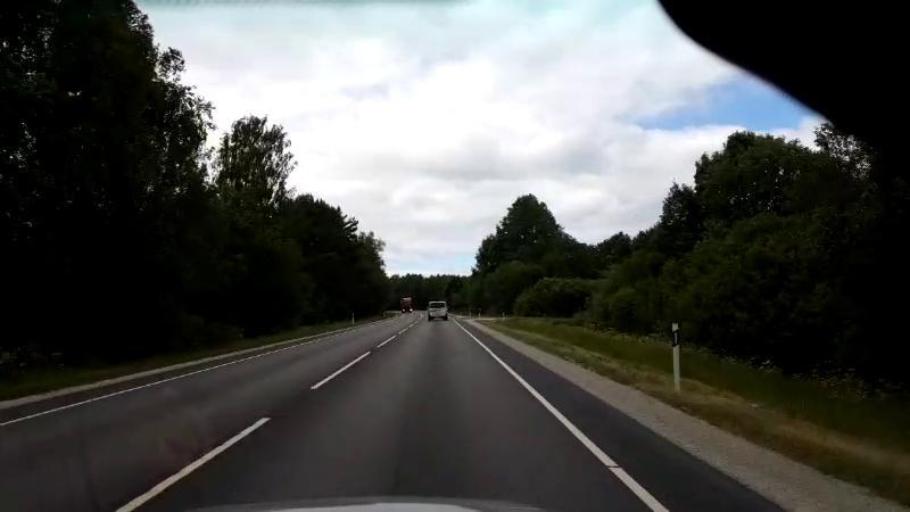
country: EE
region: Paernumaa
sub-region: Paernu linn
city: Parnu
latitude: 58.2241
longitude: 24.4917
